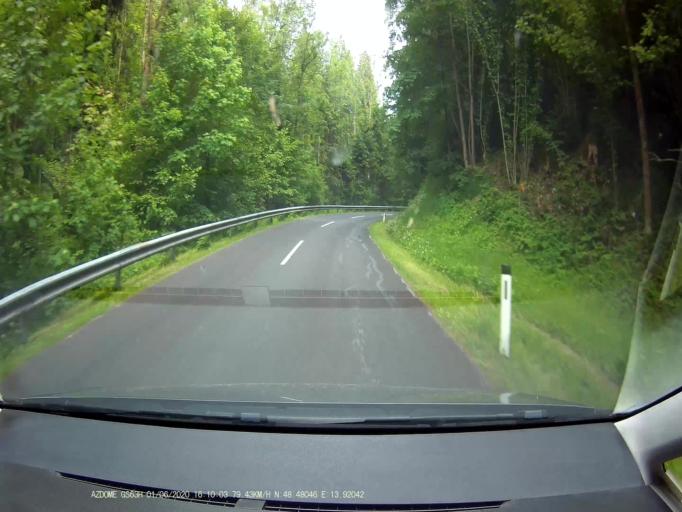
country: AT
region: Upper Austria
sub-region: Politischer Bezirk Rohrbach
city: Atzesberg
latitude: 48.4802
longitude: 13.9209
